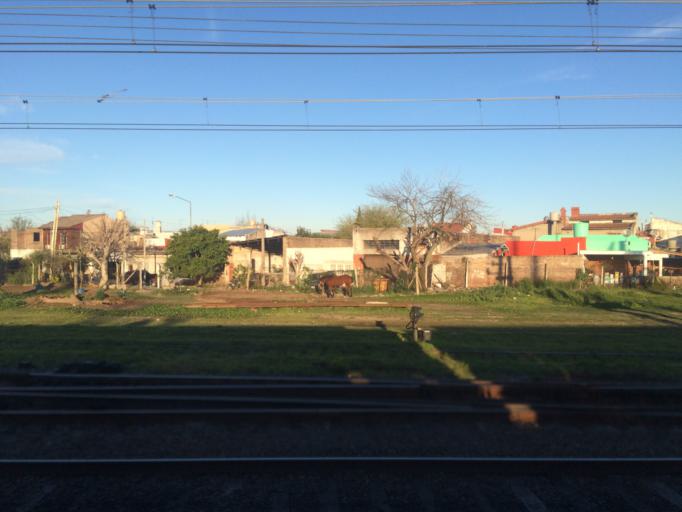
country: AR
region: Buenos Aires
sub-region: Partido de Lanus
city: Lanus
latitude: -34.6930
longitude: -58.3853
